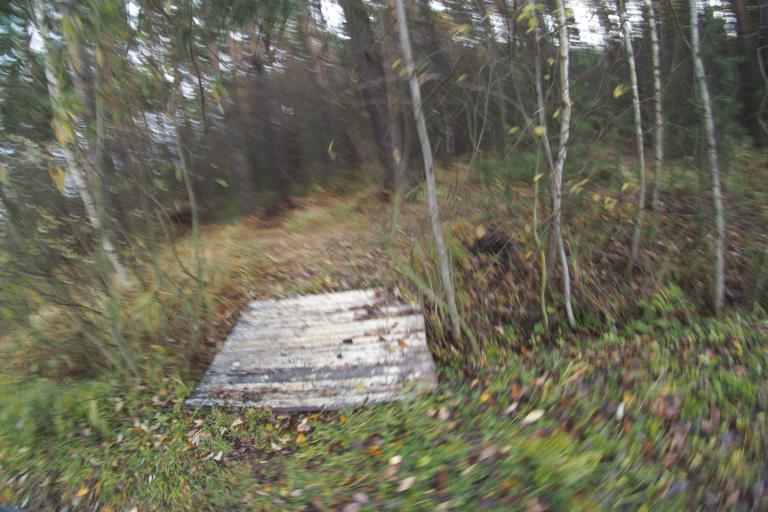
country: RU
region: Moskovskaya
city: Davydovo
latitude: 55.5809
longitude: 38.7539
